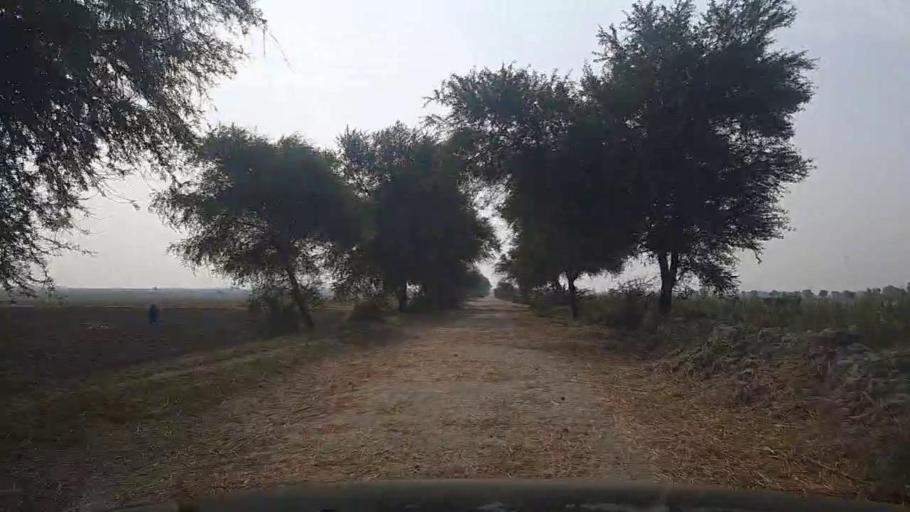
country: PK
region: Sindh
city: Bulri
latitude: 25.0204
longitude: 68.2994
